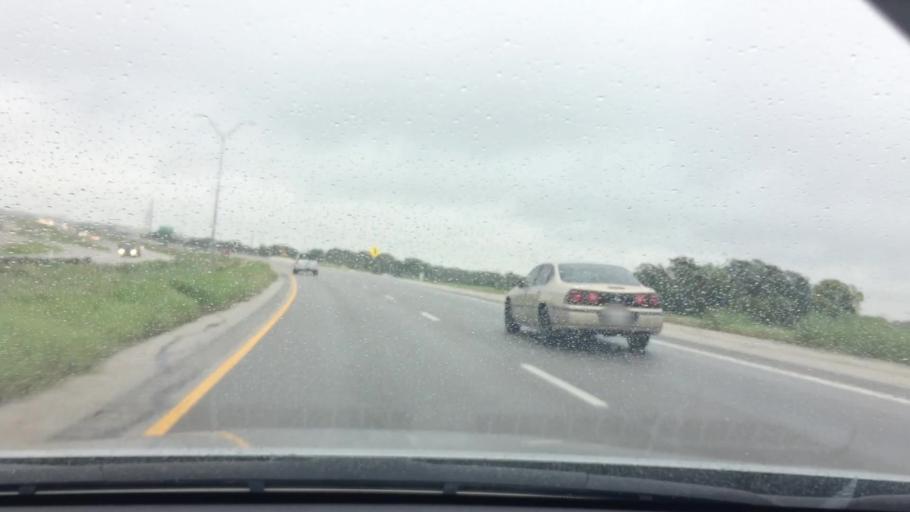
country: US
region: Texas
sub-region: Bexar County
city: Lackland Air Force Base
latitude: 29.4318
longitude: -98.6367
